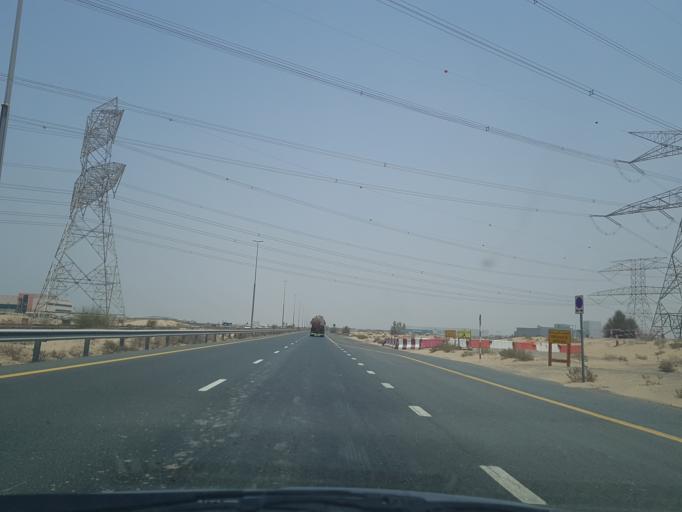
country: AE
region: Ash Shariqah
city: Sharjah
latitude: 25.1430
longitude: 55.4327
